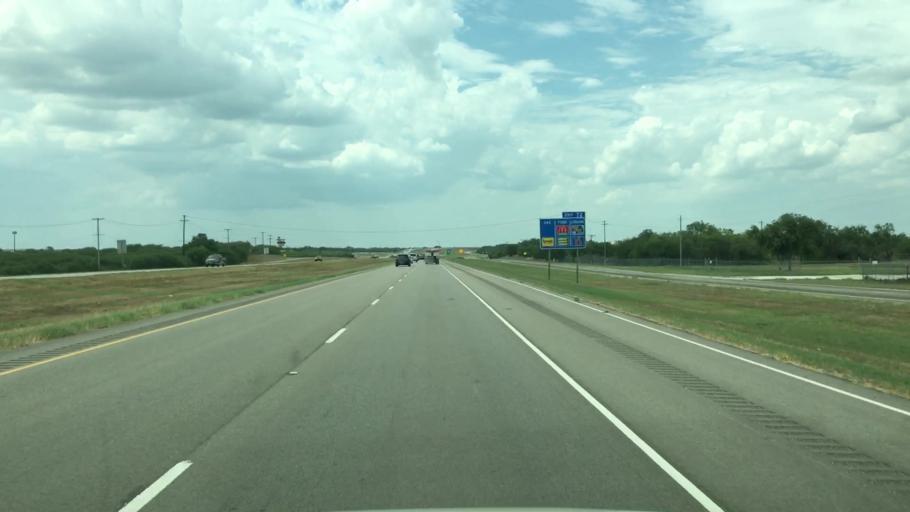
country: US
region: Texas
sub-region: Live Oak County
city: Three Rivers
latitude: 28.5149
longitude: -98.1737
